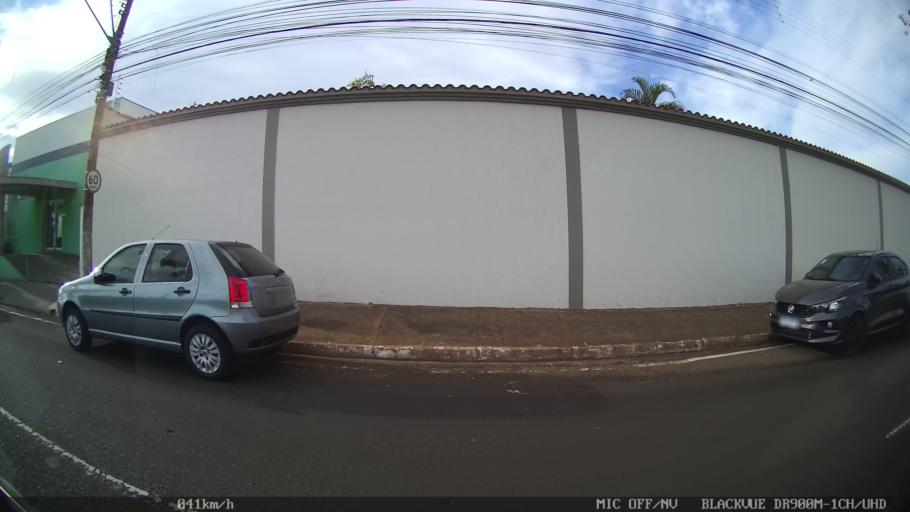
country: BR
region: Sao Paulo
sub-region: Catanduva
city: Catanduva
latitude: -21.1493
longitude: -48.9878
